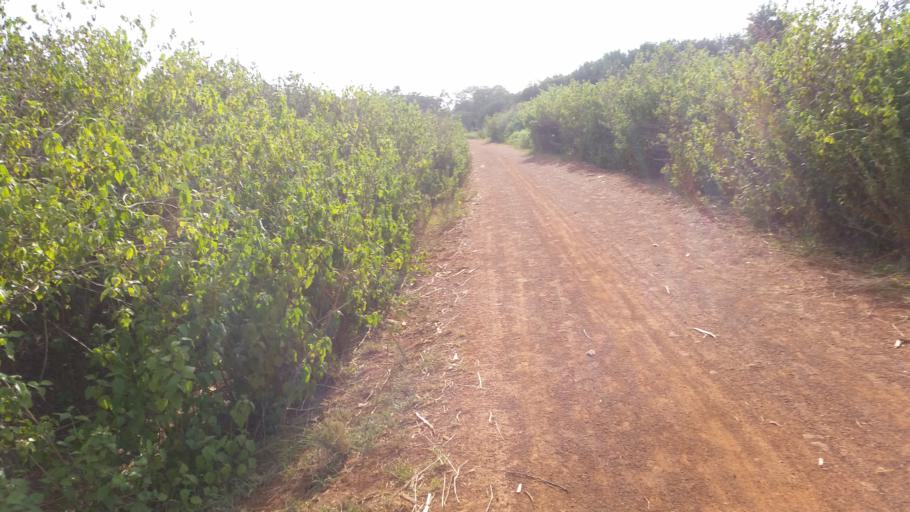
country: UG
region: Eastern Region
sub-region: Busia District
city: Busia
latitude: 0.5506
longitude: 33.9875
